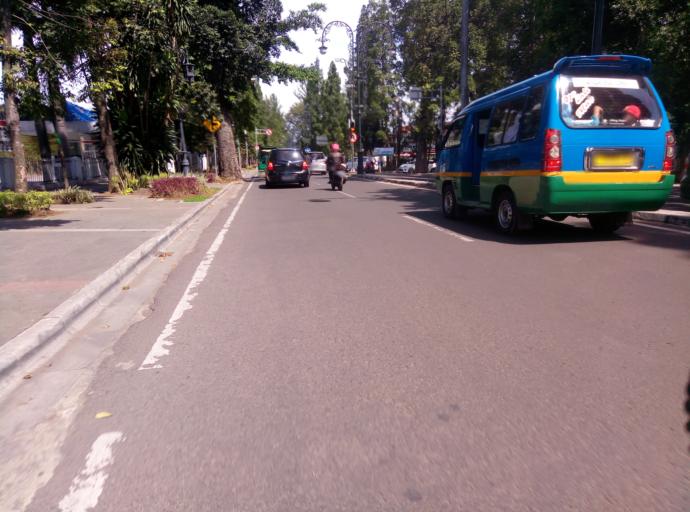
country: ID
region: West Java
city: Bandung
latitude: -6.8868
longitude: 107.6137
